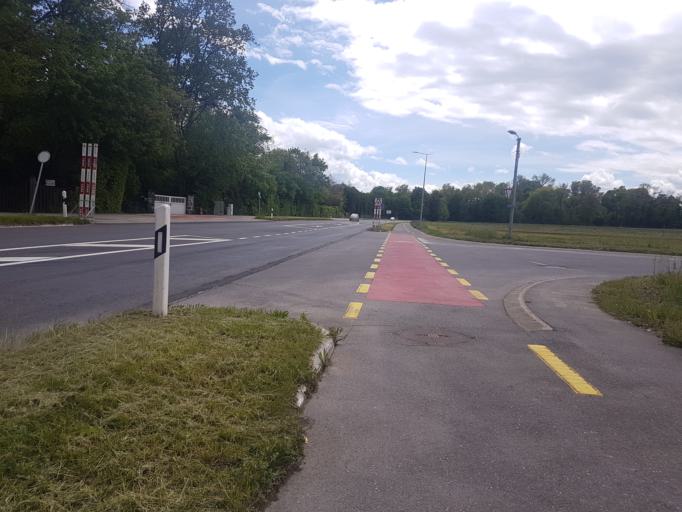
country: CH
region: Vaud
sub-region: Nyon District
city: Founex
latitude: 46.3430
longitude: 6.2055
